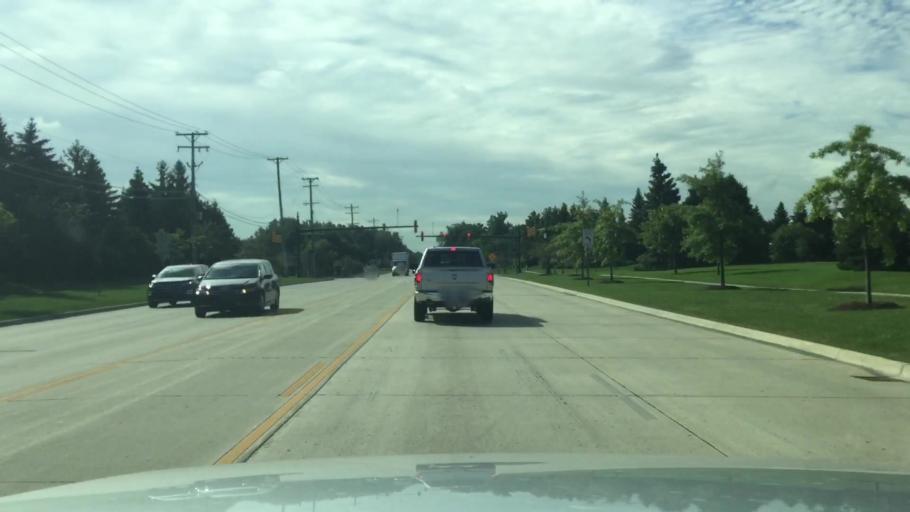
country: US
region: Michigan
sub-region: Wayne County
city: Canton
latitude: 42.2941
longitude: -83.4866
